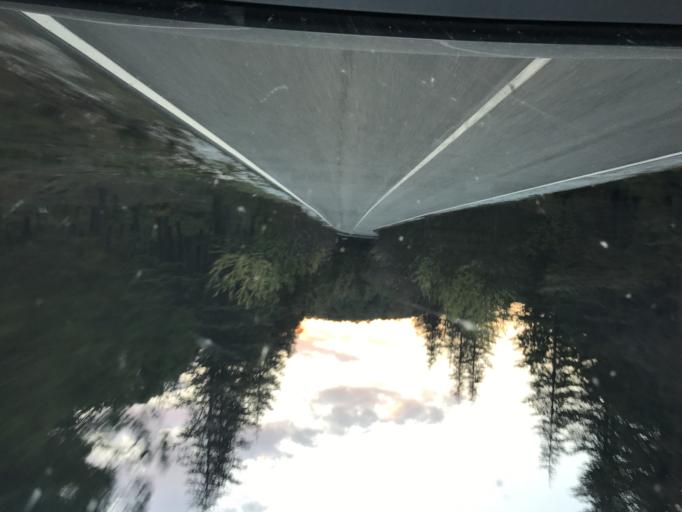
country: ES
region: Andalusia
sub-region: Provincia de Granada
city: Beas de Granada
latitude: 37.2554
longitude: -3.4832
